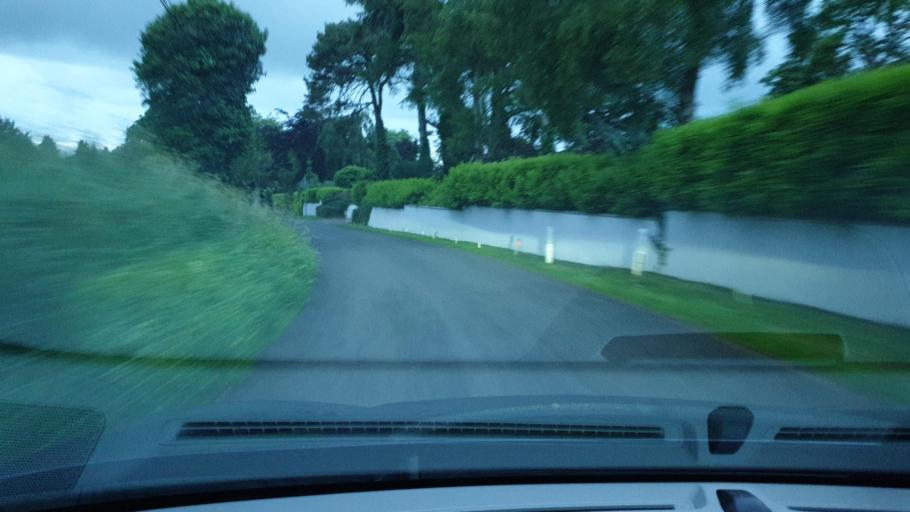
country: IE
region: Leinster
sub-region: An Mhi
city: Ashbourne
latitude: 53.5031
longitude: -6.3644
